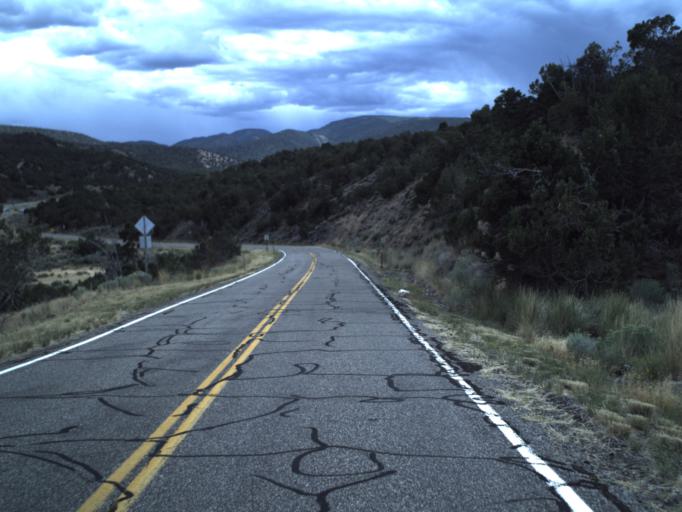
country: US
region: Utah
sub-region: Sevier County
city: Aurora
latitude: 38.7748
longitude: -111.9309
